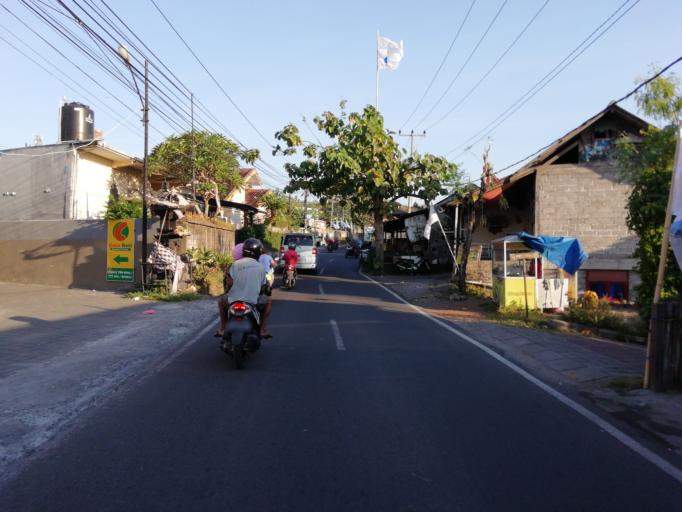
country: ID
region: Bali
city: Bualu
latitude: -8.7895
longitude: 115.1961
